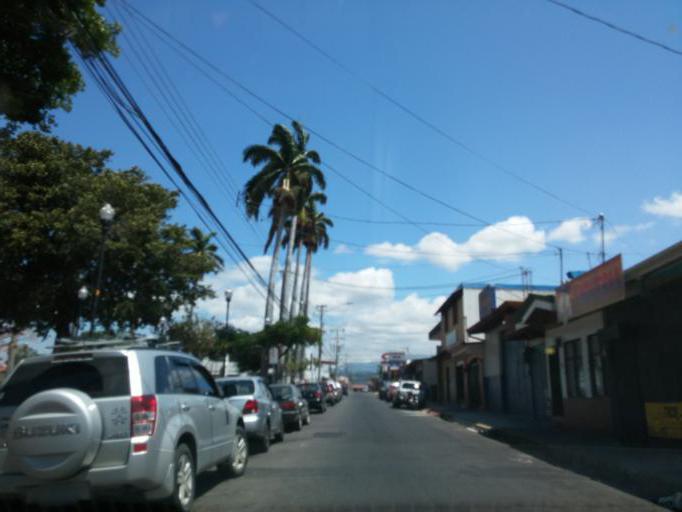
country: CR
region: Alajuela
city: Alajuela
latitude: 10.0168
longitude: -84.2181
